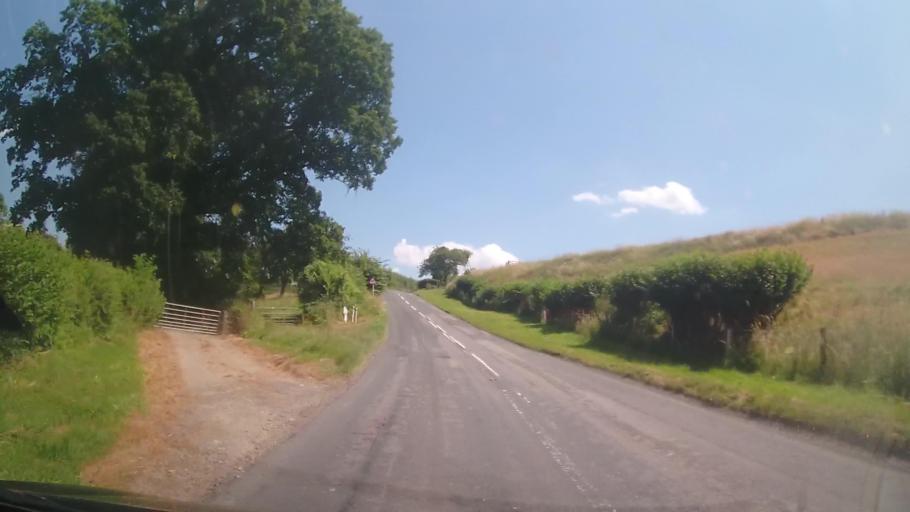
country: GB
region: England
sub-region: Herefordshire
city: Brockhampton
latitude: 52.0038
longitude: -2.6019
